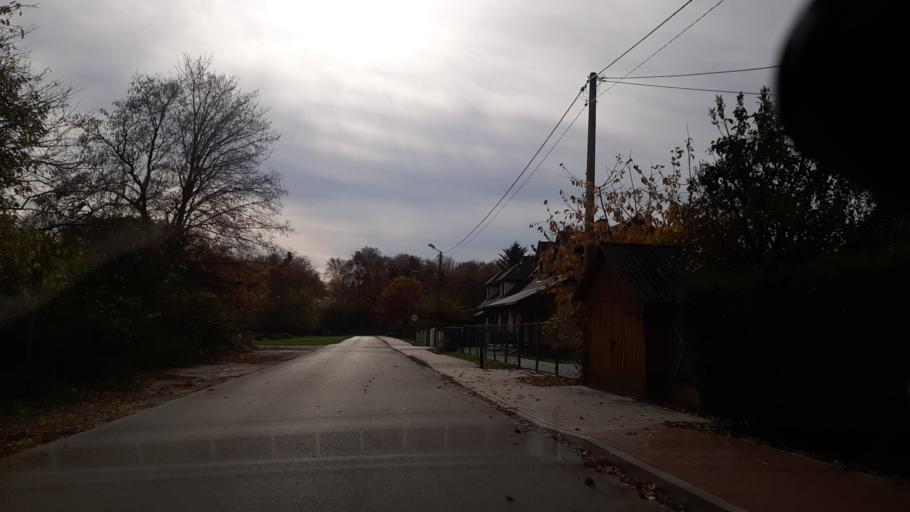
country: PL
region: Lublin Voivodeship
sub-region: Powiat pulawski
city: Markuszow
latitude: 51.3624
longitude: 22.2911
